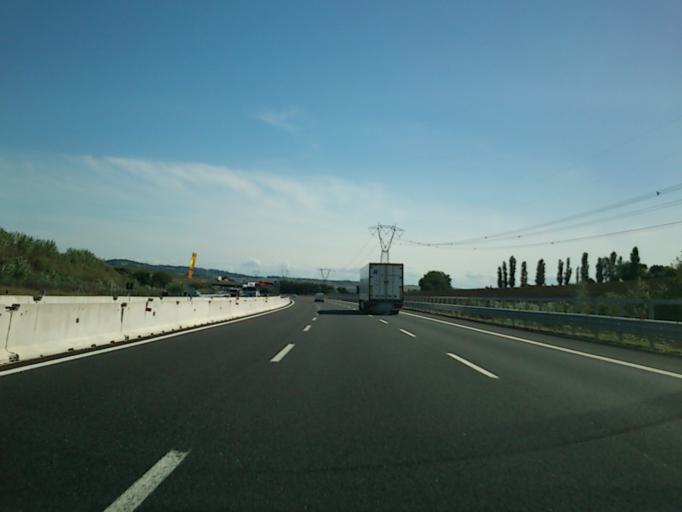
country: IT
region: The Marches
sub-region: Provincia di Pesaro e Urbino
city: Borgo Santa Maria
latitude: 43.9096
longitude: 12.8214
